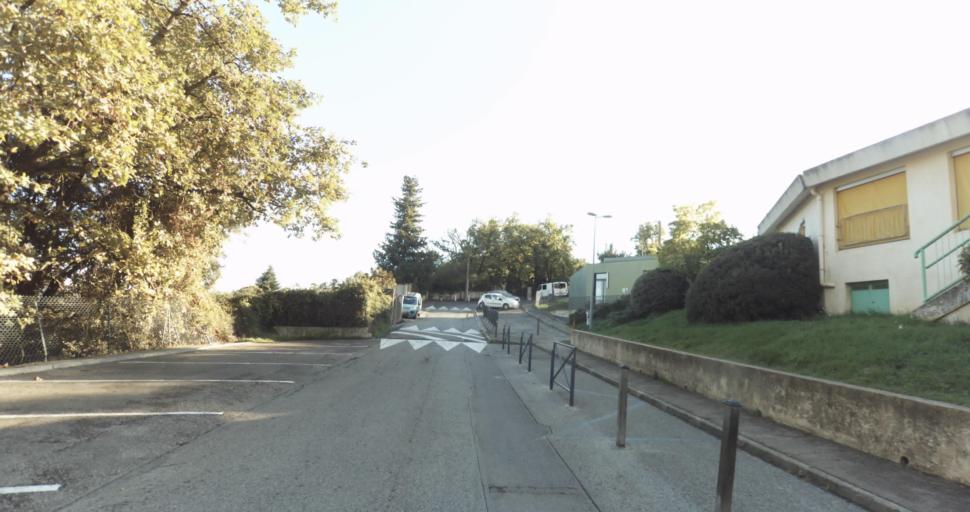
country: FR
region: Provence-Alpes-Cote d'Azur
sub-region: Departement des Alpes-Maritimes
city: Vence
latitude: 43.7266
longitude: 7.1237
